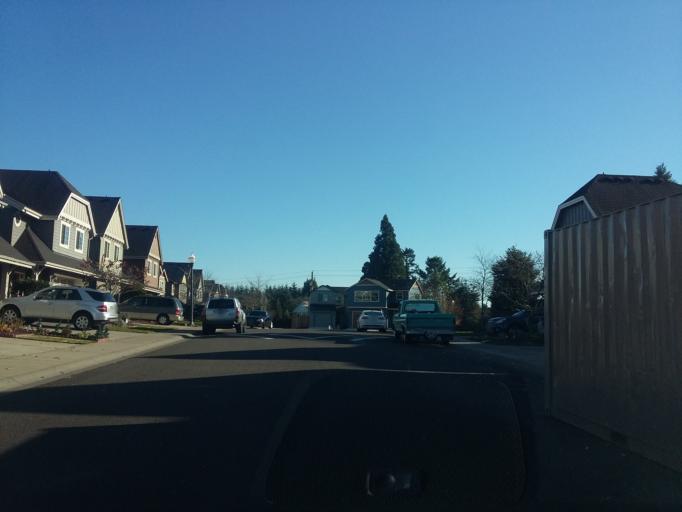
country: US
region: Washington
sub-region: Clark County
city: Barberton
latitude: 45.6888
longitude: -122.6237
